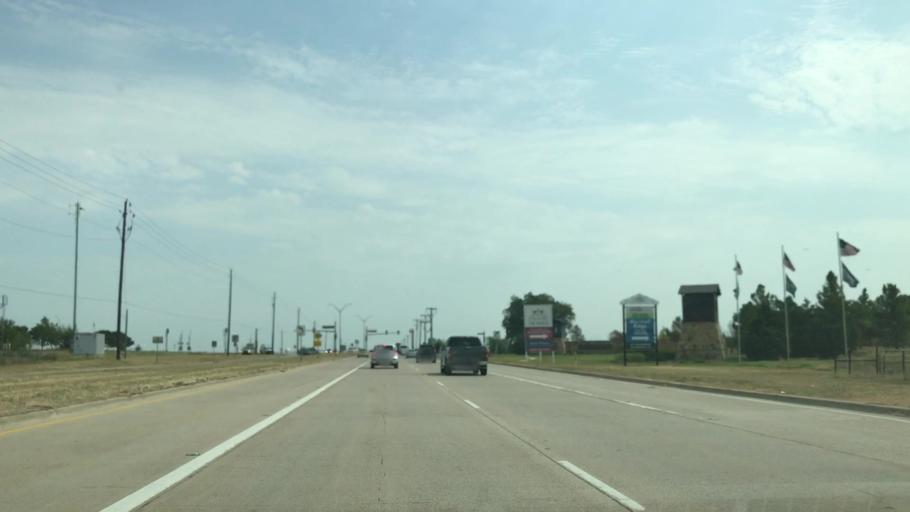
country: US
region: Texas
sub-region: Tarrant County
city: Keller
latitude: 32.9692
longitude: -97.2469
